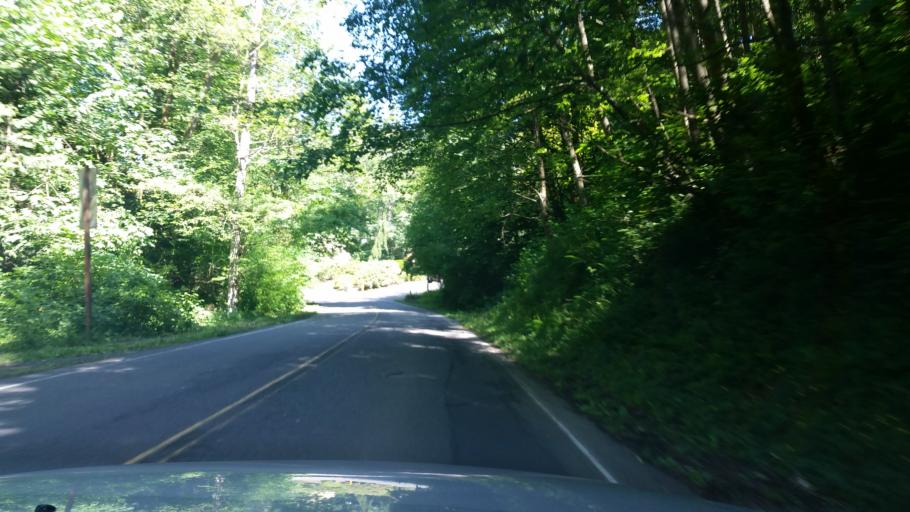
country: US
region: Washington
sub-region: King County
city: Lake Forest Park
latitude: 47.7602
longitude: -122.2975
